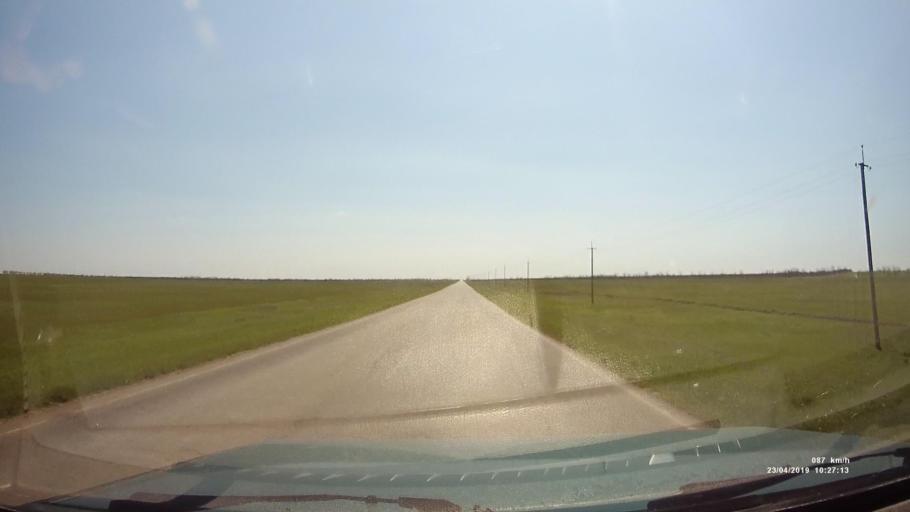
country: RU
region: Kalmykiya
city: Yashalta
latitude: 46.6155
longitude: 42.4875
